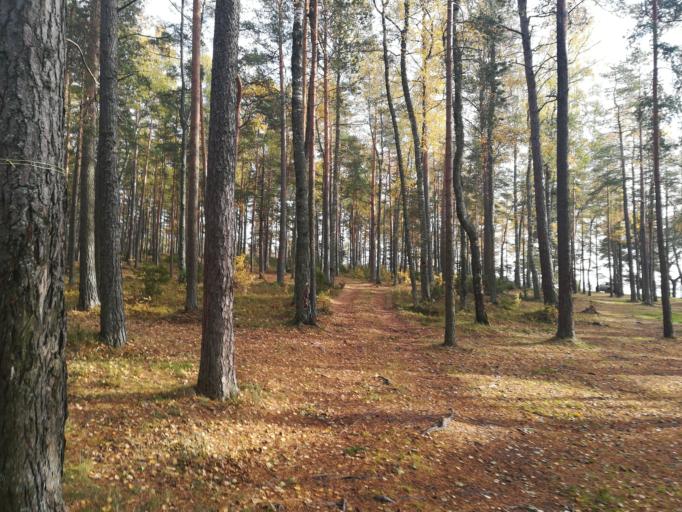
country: RU
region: Leningrad
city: Ust'-Luga
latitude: 59.7518
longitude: 28.1501
